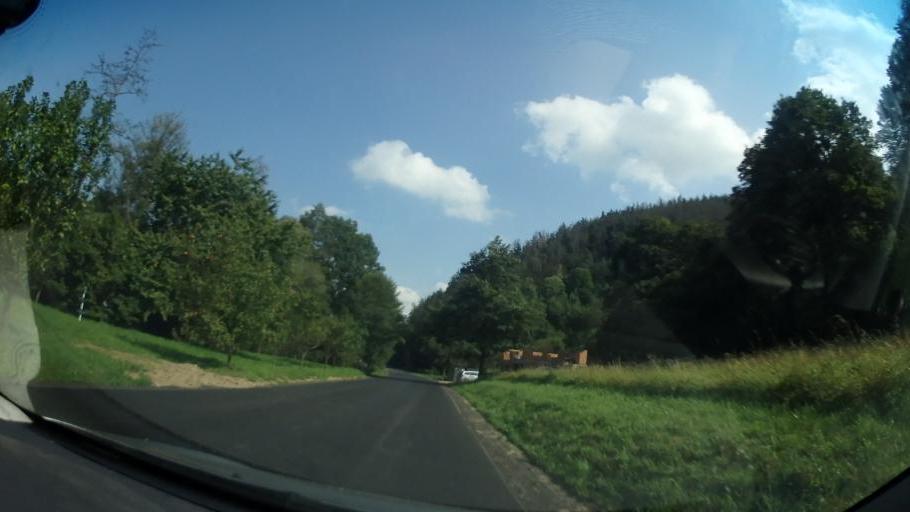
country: CZ
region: South Moravian
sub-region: Okres Brno-Venkov
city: Nedvedice
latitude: 49.5296
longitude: 16.3507
